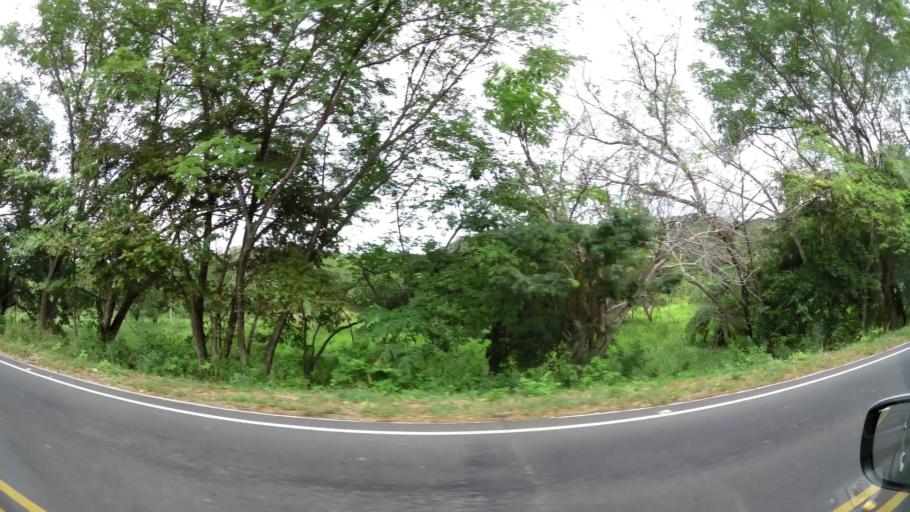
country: CR
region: Guanacaste
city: Nandayure
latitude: 10.2487
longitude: -85.2272
